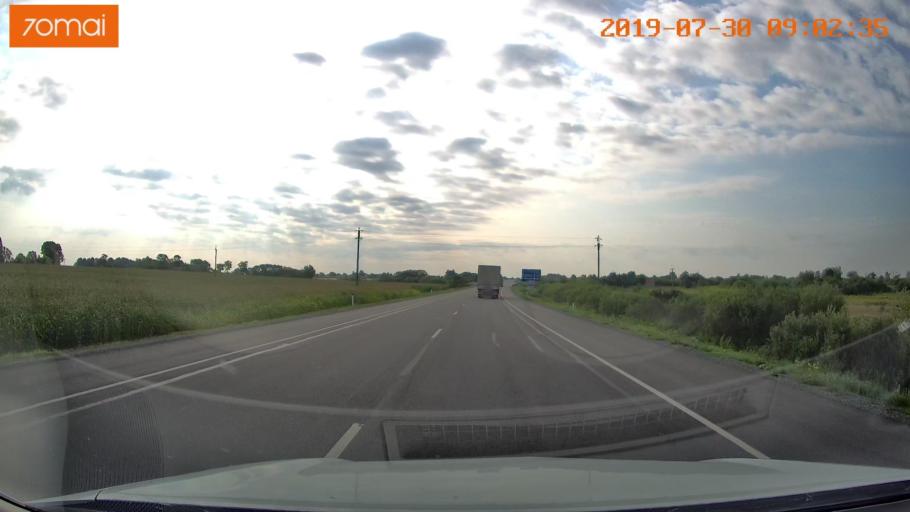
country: RU
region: Kaliningrad
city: Gusev
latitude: 54.6146
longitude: 22.2360
